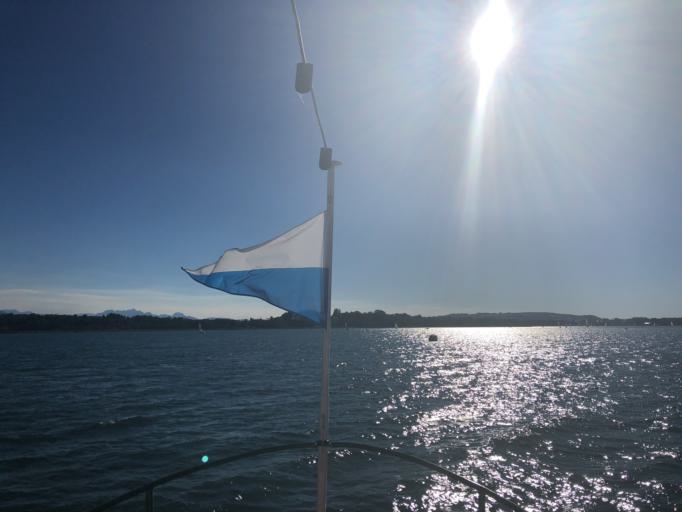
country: DE
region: Bavaria
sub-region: Upper Bavaria
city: Chiemsee
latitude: 47.8709
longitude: 12.4163
